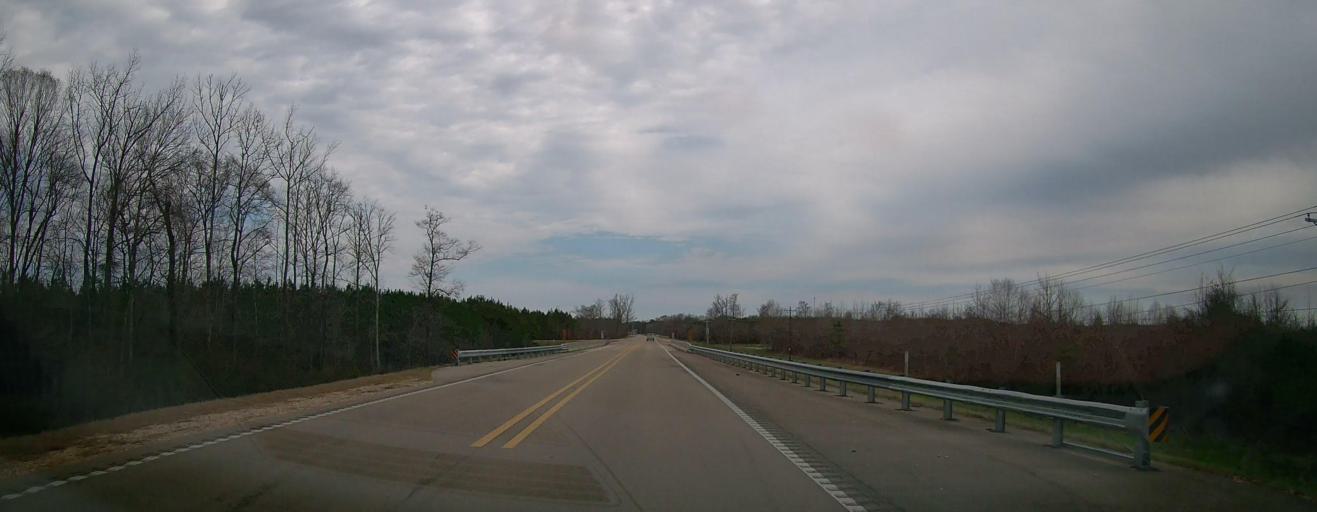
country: US
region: Mississippi
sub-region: Itawamba County
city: Fulton
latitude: 34.2431
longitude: -88.2811
